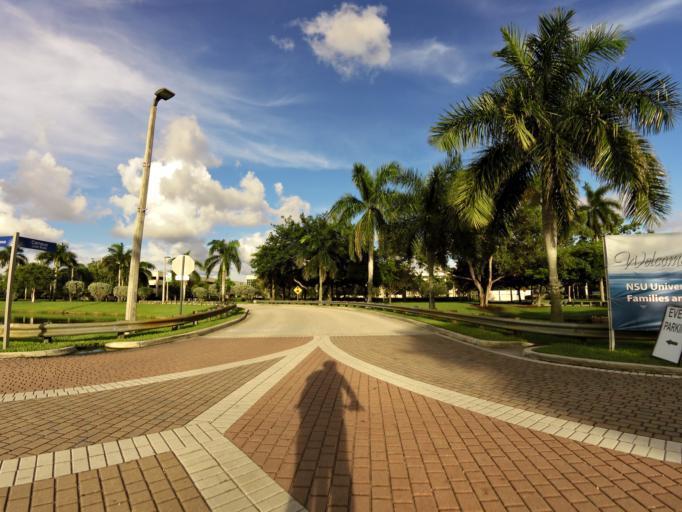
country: US
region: Florida
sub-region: Broward County
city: Davie
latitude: 26.0811
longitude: -80.2458
